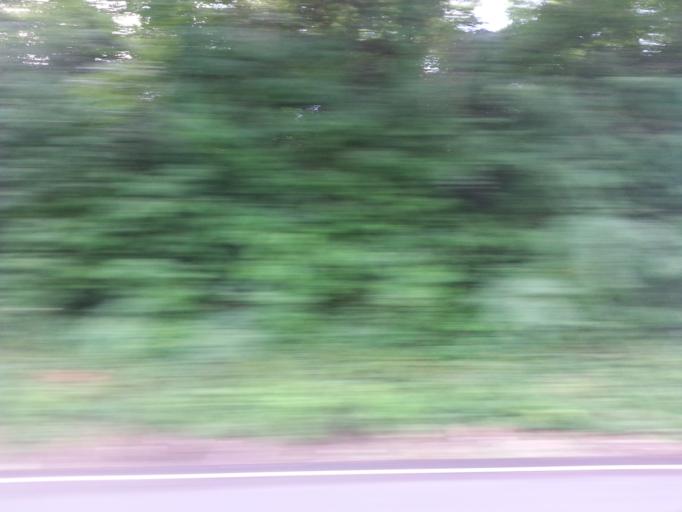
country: US
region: Tennessee
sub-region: Knox County
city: Knoxville
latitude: 35.9309
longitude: -83.9892
